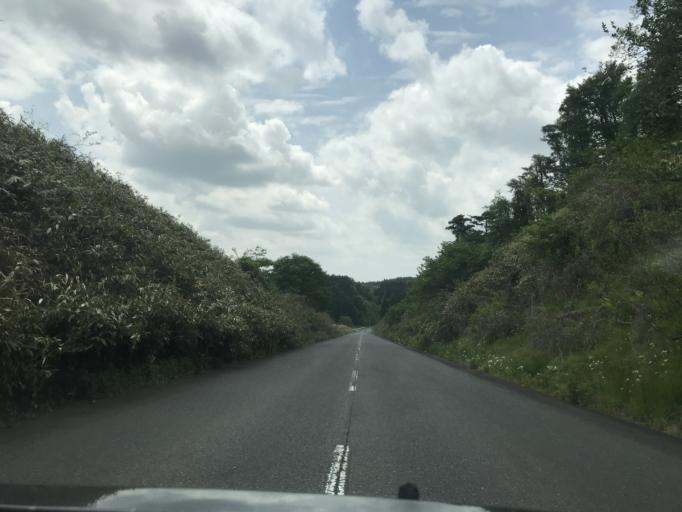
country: JP
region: Miyagi
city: Furukawa
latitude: 38.7180
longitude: 140.9197
